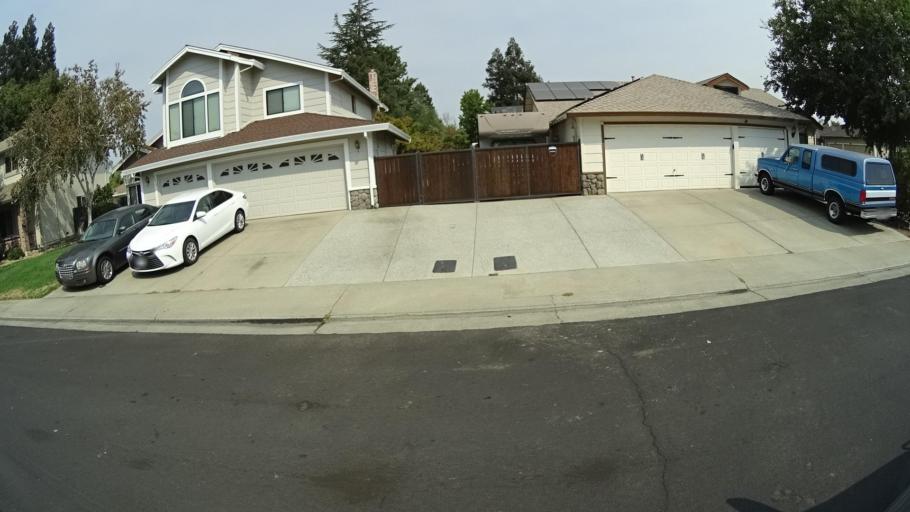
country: US
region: California
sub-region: Sacramento County
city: Elk Grove
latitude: 38.4274
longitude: -121.3747
